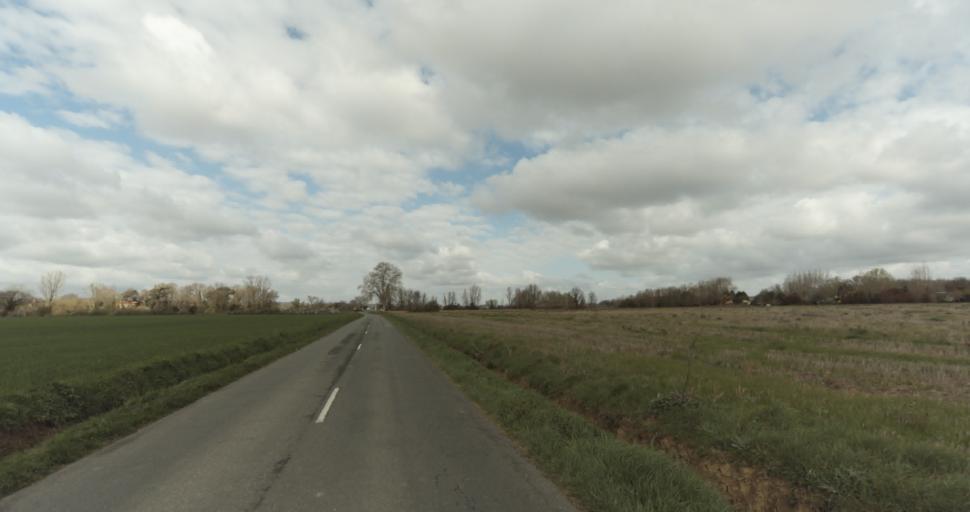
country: FR
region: Midi-Pyrenees
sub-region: Departement de la Haute-Garonne
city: Auterive
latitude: 43.3592
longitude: 1.4496
